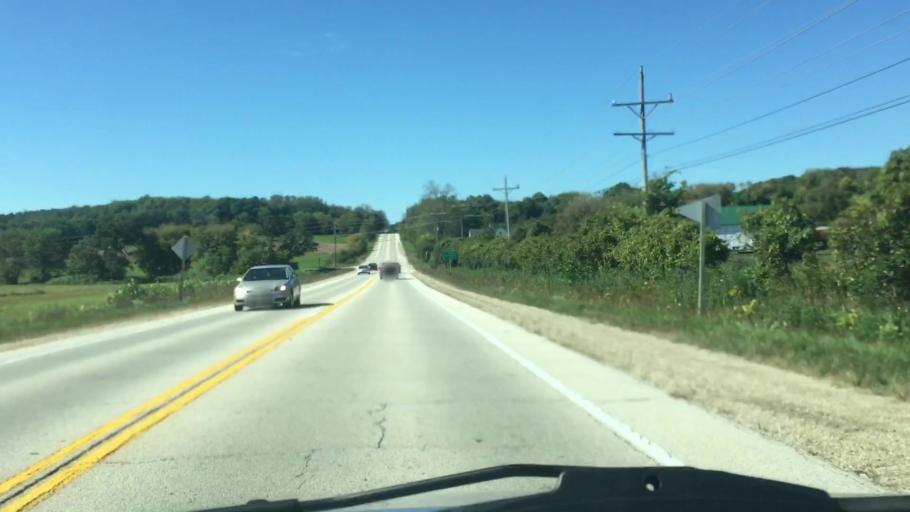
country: US
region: Wisconsin
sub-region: Waukesha County
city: Wales
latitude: 43.0208
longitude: -88.3064
